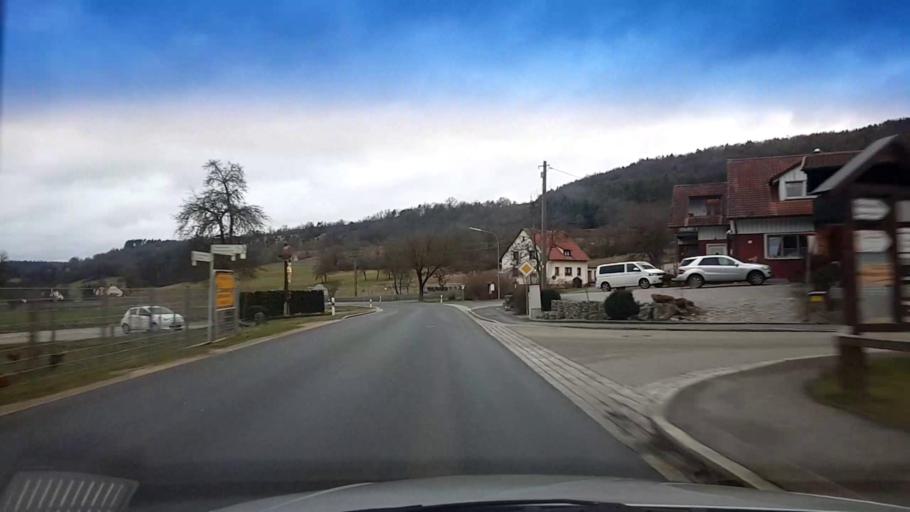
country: DE
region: Bavaria
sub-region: Upper Franconia
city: Wattendorf
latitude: 50.0646
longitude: 11.0709
